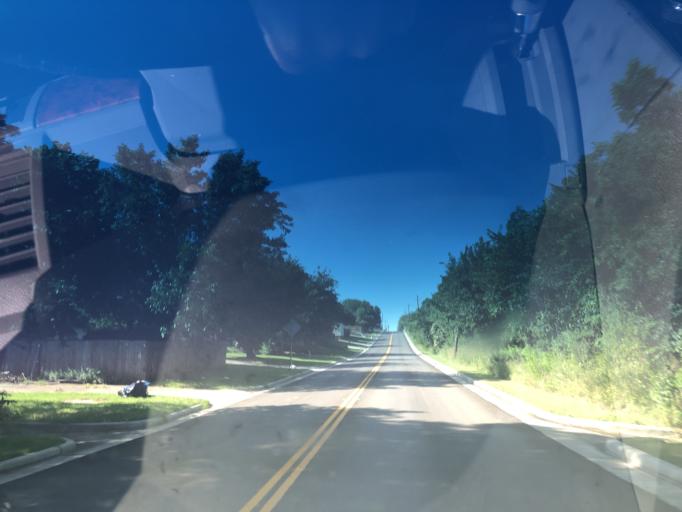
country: US
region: Texas
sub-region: Dallas County
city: Grand Prairie
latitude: 32.7192
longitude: -97.0197
